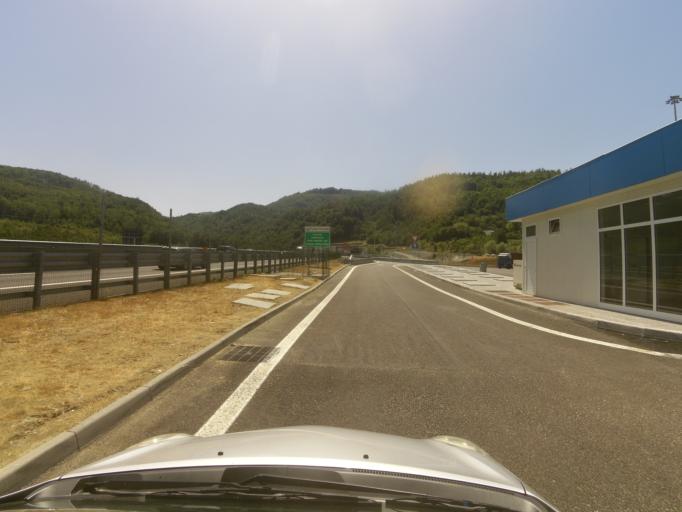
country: IT
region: Emilia-Romagna
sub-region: Provincia di Bologna
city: Castiglione dei Pepoli
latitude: 44.1499
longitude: 11.1937
